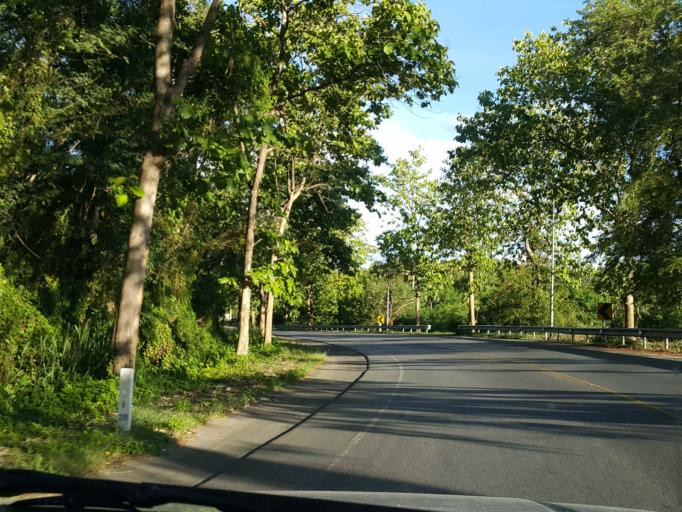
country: TH
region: Chiang Mai
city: Chom Thong
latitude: 18.4816
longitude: 98.6697
